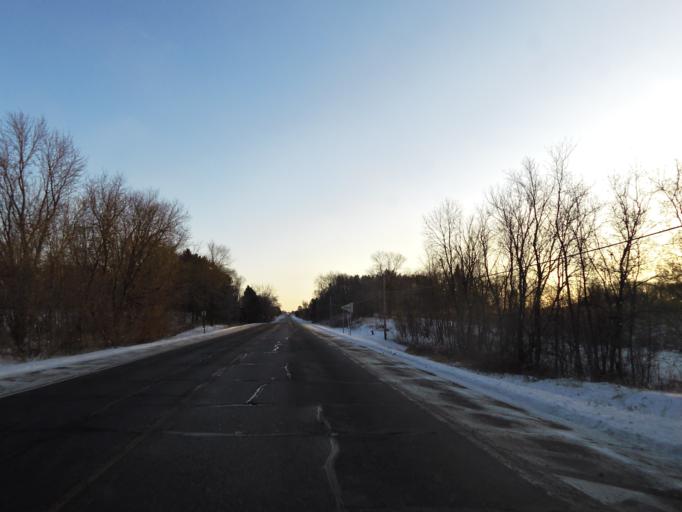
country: US
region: Minnesota
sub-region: Washington County
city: Lake Elmo
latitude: 44.9724
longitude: -92.8830
